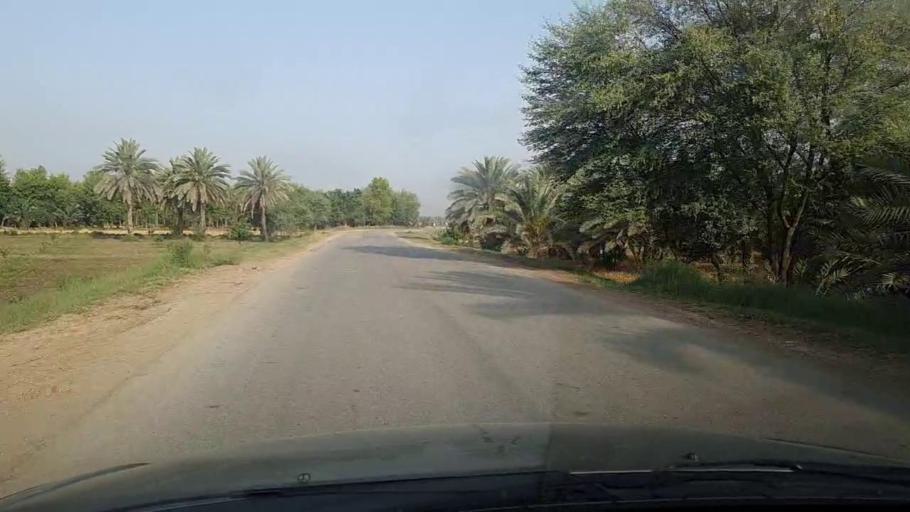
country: PK
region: Sindh
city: Pir jo Goth
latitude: 27.5620
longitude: 68.6600
